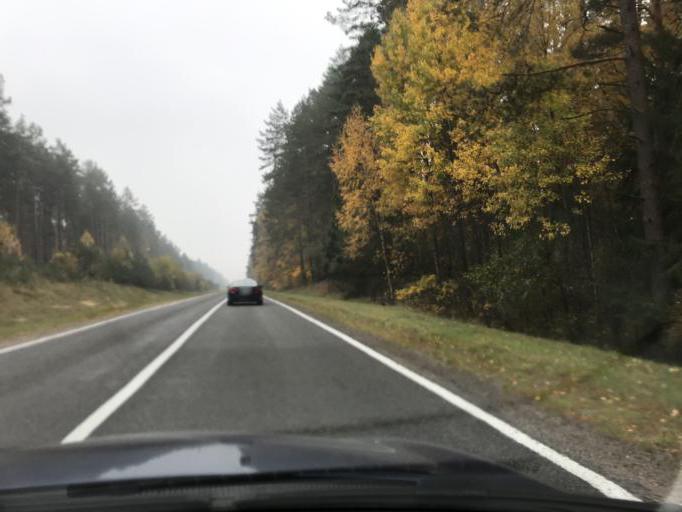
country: LT
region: Alytaus apskritis
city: Druskininkai
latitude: 53.8694
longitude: 23.8945
